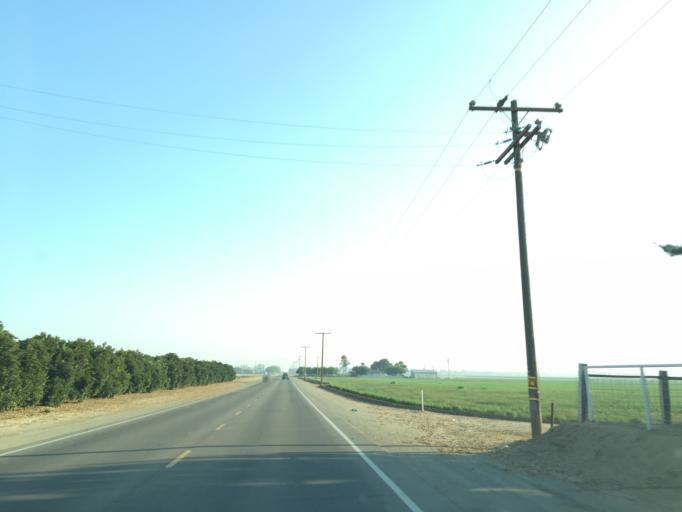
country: US
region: California
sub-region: Tulare County
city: Cutler
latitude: 36.4456
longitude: -119.2777
